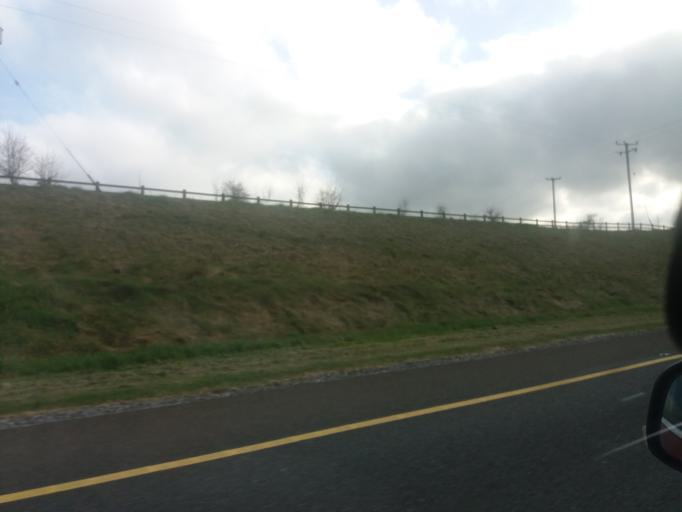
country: IE
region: Munster
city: Nenagh Bridge
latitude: 52.8750
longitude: -8.0222
